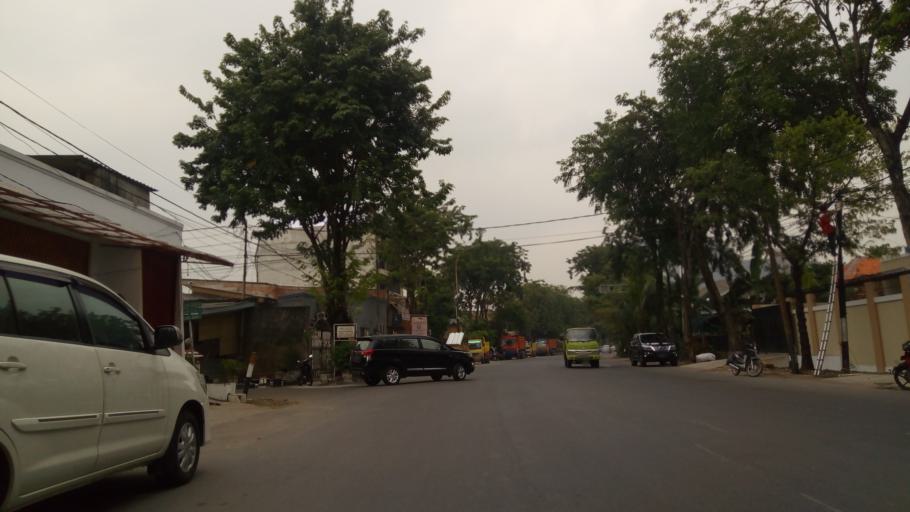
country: ID
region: Jakarta Raya
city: Jakarta
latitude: -6.1462
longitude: 106.8430
